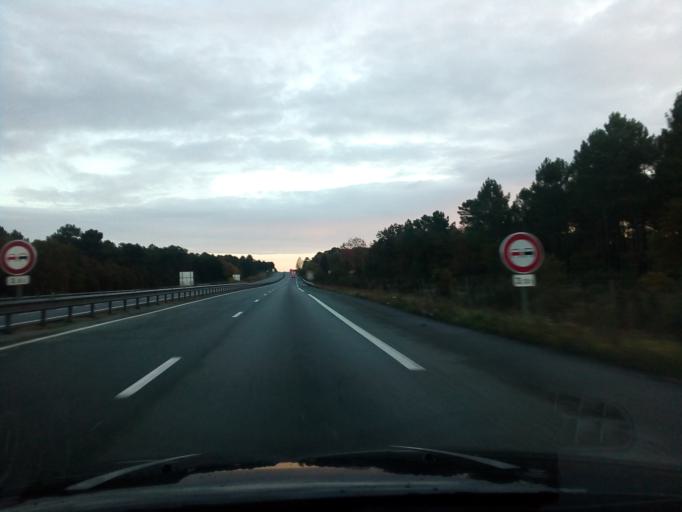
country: FR
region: Aquitaine
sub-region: Departement de la Gironde
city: Laruscade
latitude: 45.1764
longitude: -0.3287
